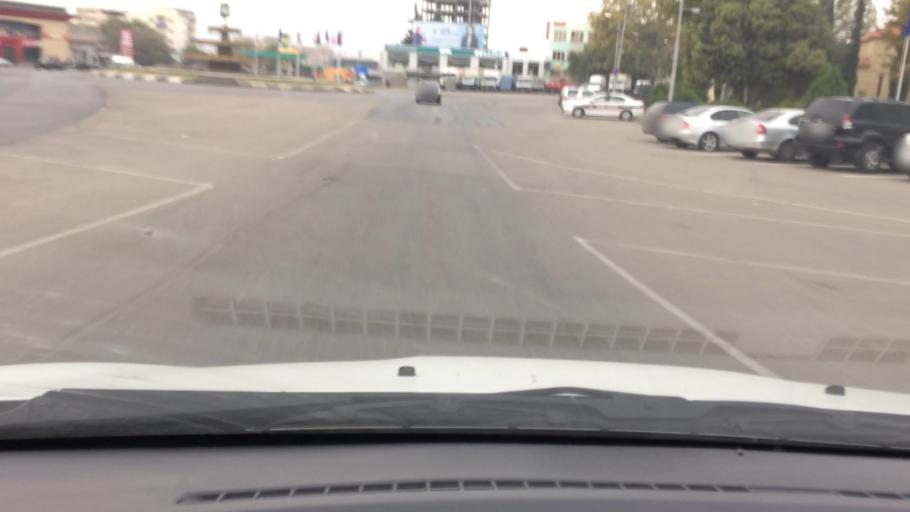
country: GE
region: Kvemo Kartli
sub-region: Marneuli
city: Marneuli
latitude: 41.4882
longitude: 44.7988
